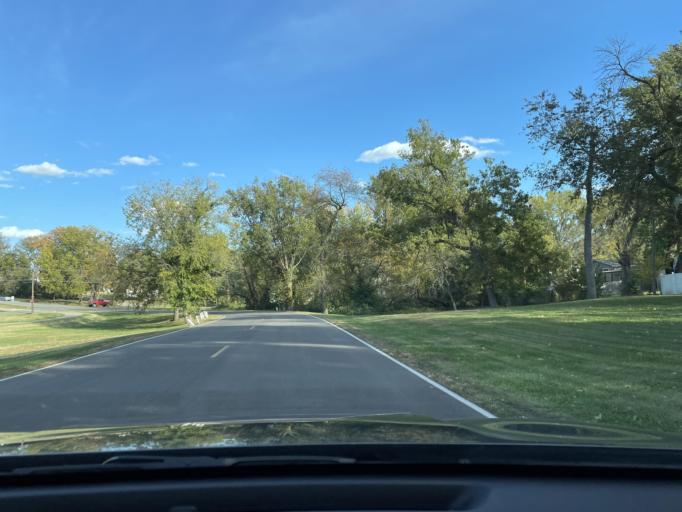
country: US
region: Missouri
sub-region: Buchanan County
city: Saint Joseph
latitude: 39.7276
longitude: -94.8407
